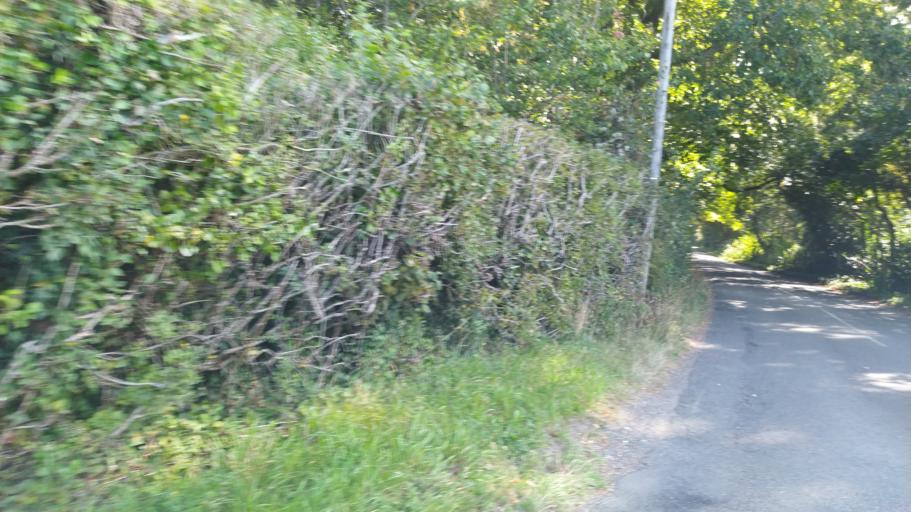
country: GB
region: England
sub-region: Hampshire
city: Havant
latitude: 50.9063
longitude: -0.9623
